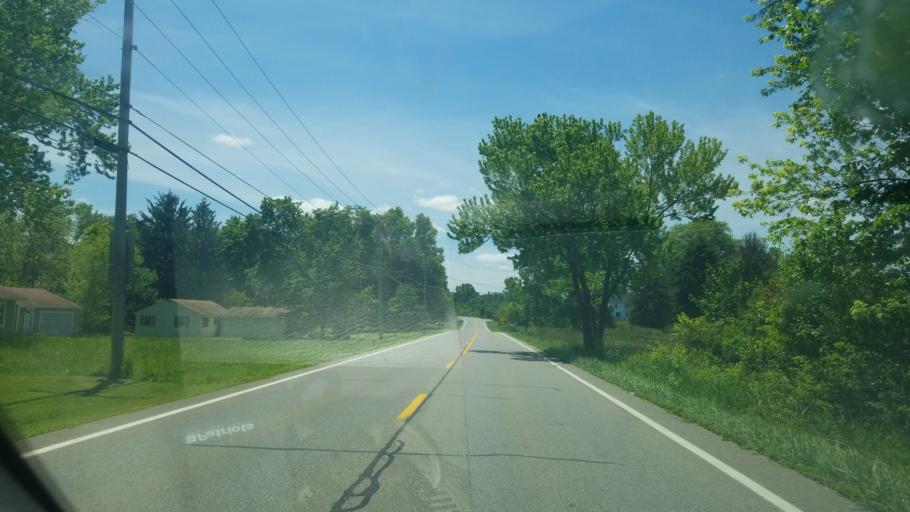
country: US
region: Ohio
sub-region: Columbiana County
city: Columbiana
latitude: 40.9270
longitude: -80.6539
